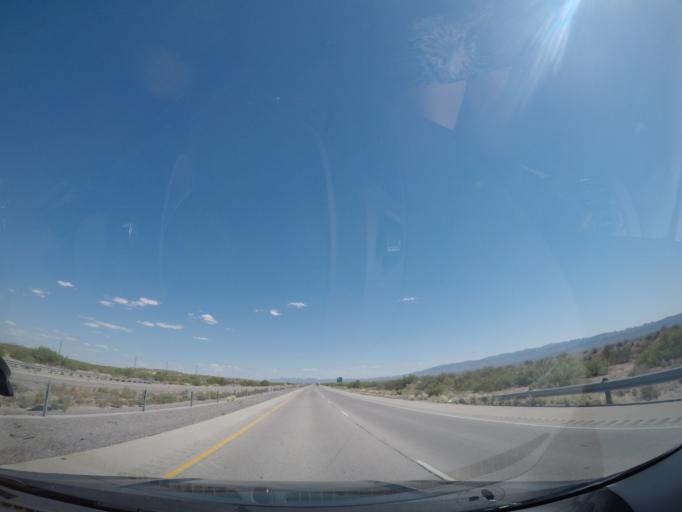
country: US
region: Texas
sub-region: Hudspeth County
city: Fort Hancock
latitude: 31.2690
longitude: -105.7946
